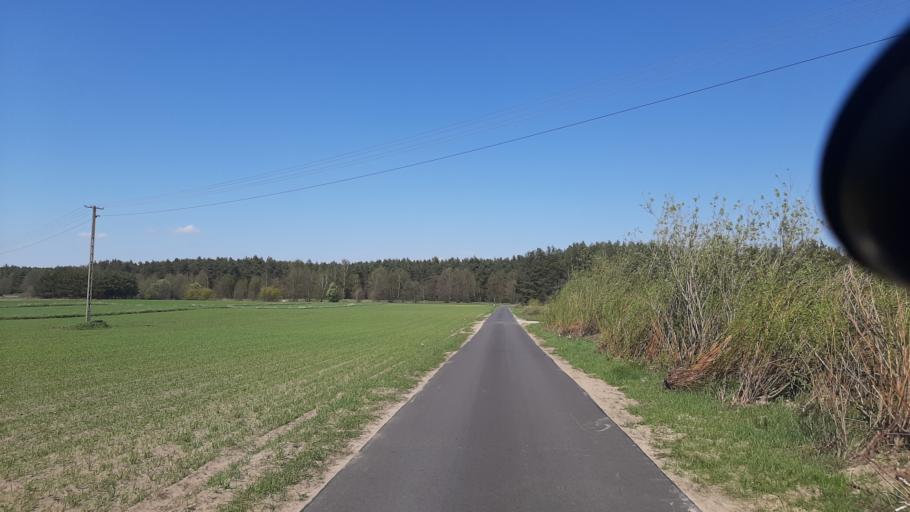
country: PL
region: Lublin Voivodeship
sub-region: Powiat lubelski
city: Garbow
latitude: 51.4054
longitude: 22.3226
